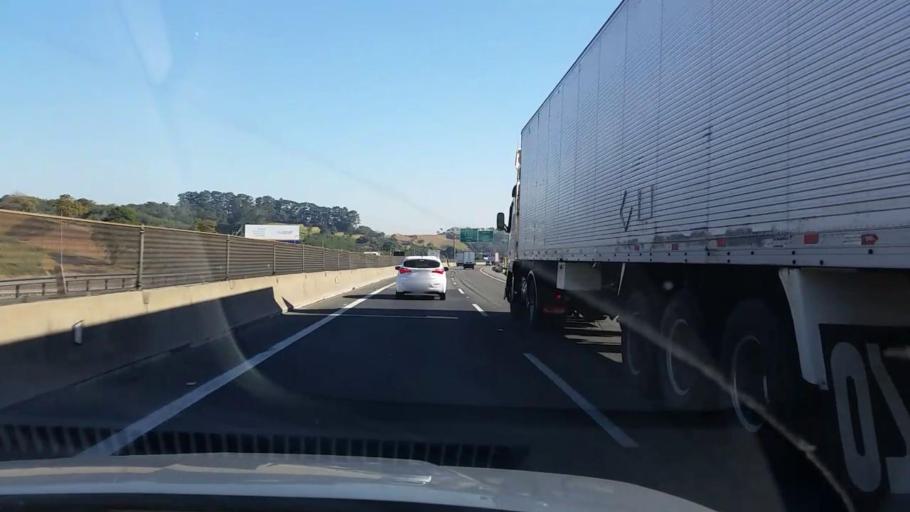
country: BR
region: Sao Paulo
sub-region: Jundiai
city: Jundiai
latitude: -23.2073
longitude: -46.8976
